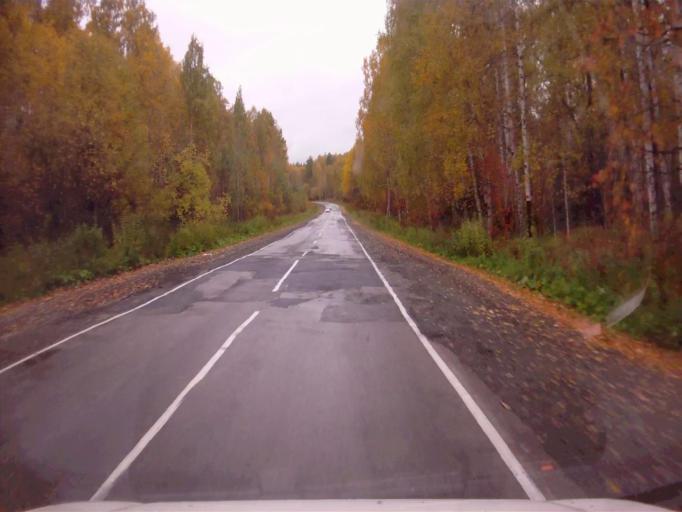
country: RU
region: Chelyabinsk
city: Nizhniy Ufaley
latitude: 56.0536
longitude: 59.9542
